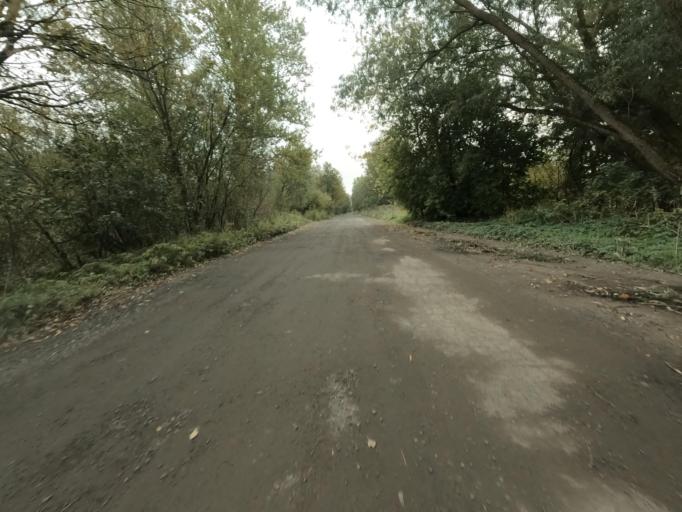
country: RU
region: St.-Petersburg
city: Sapernyy
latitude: 59.7647
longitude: 30.6430
